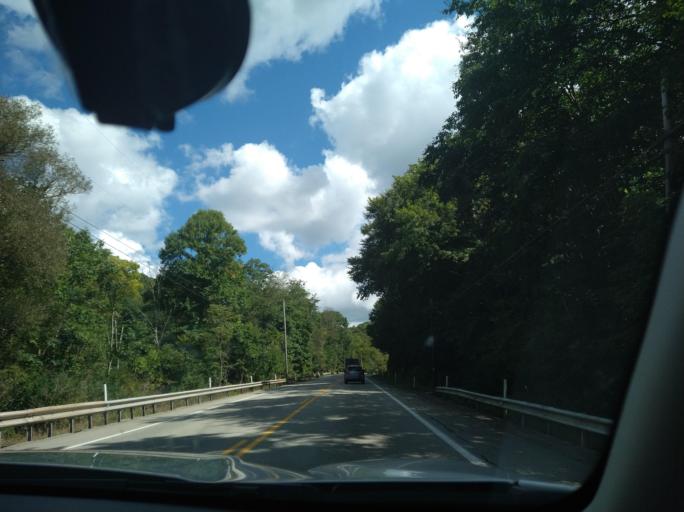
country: US
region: Pennsylvania
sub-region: Fayette County
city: Bear Rocks
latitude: 40.0736
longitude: -79.2968
